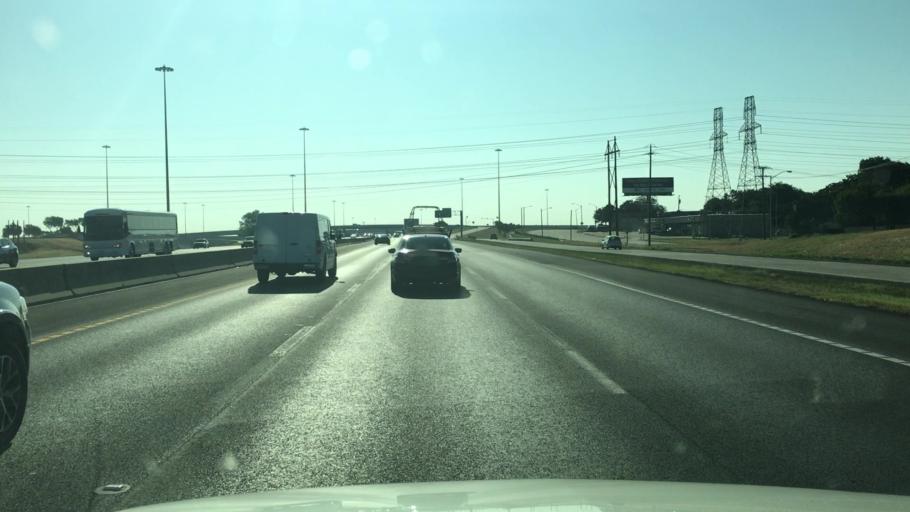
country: US
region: Texas
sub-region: Tarrant County
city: Richland Hills
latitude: 32.7597
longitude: -97.2236
